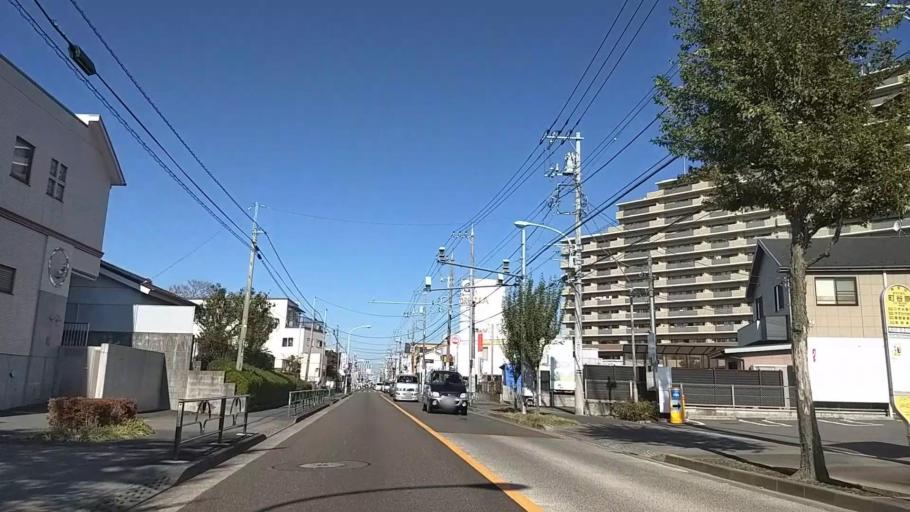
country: JP
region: Tokyo
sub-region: Machida-shi
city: Machida
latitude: 35.5230
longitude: 139.4692
